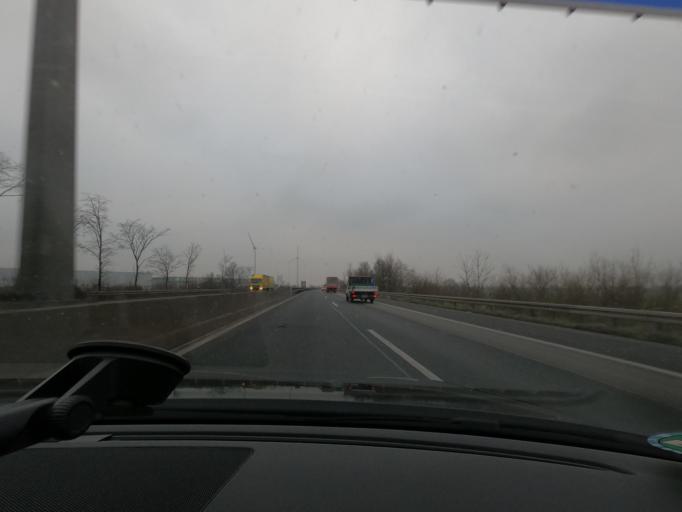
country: DE
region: North Rhine-Westphalia
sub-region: Regierungsbezirk Dusseldorf
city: Juchen
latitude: 51.1141
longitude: 6.4292
